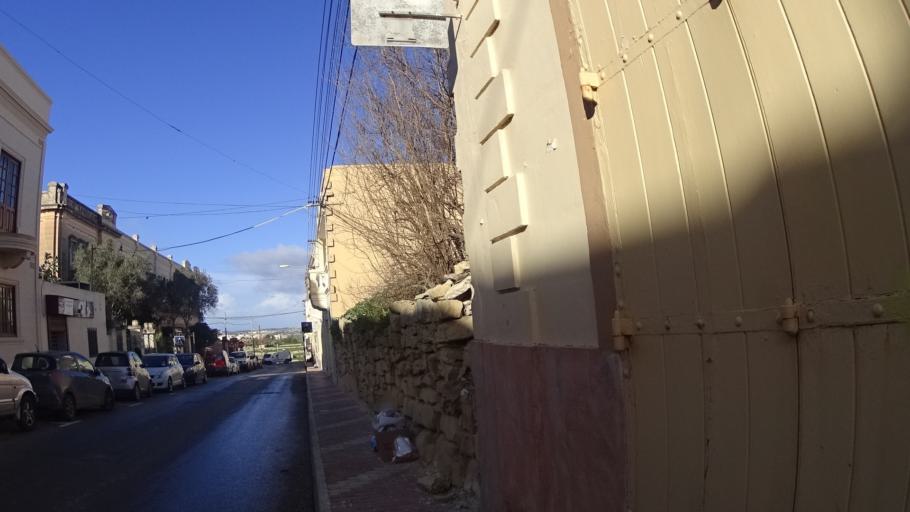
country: MT
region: Hal Gharghur
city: Hal Gharghur
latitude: 35.9241
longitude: 14.4524
